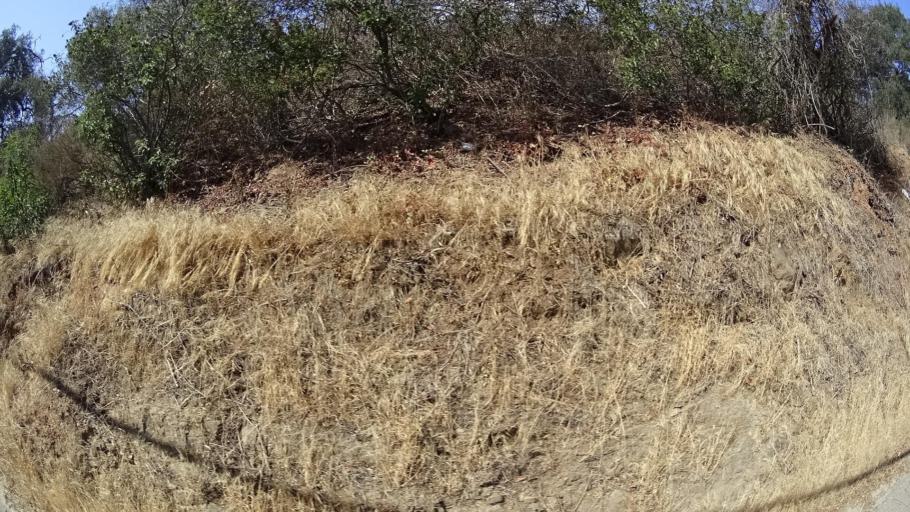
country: US
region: California
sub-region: San Diego County
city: San Marcos
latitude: 33.1913
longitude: -117.1561
